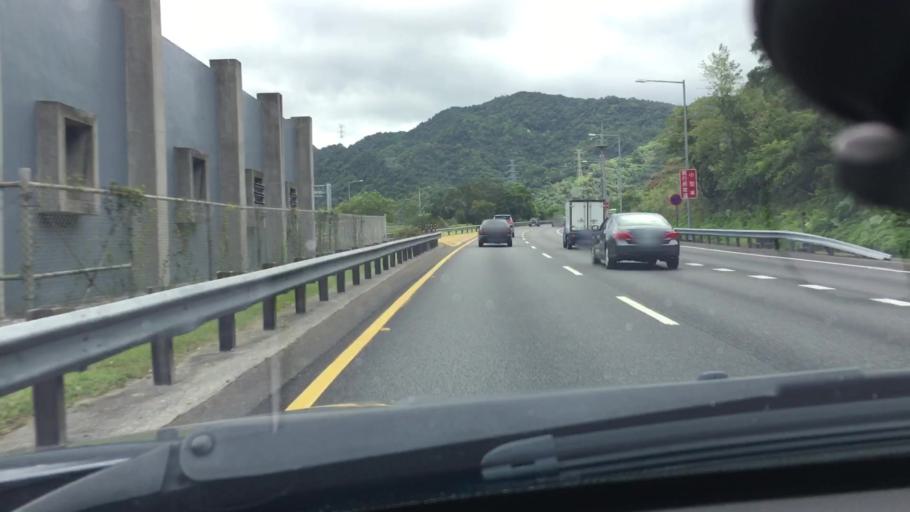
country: TW
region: Taipei
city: Taipei
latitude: 24.9820
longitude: 121.6672
